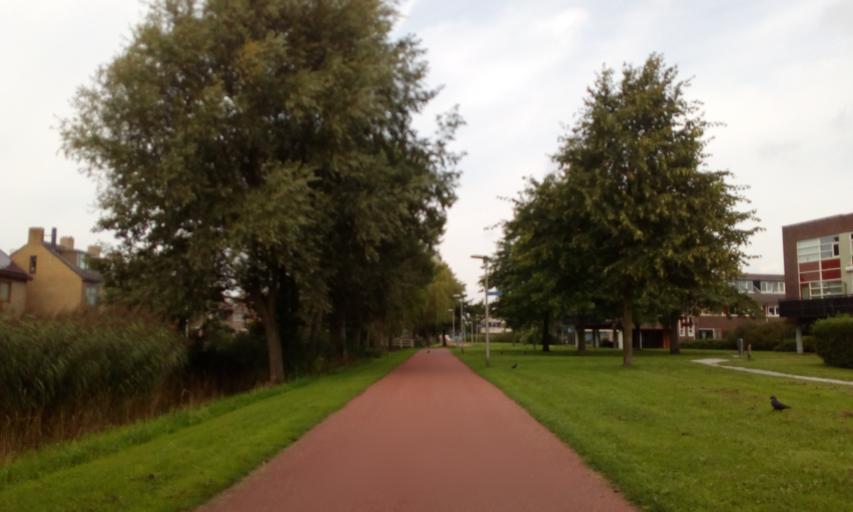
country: NL
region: South Holland
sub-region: Gemeente Den Haag
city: Ypenburg
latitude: 52.0490
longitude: 4.4020
